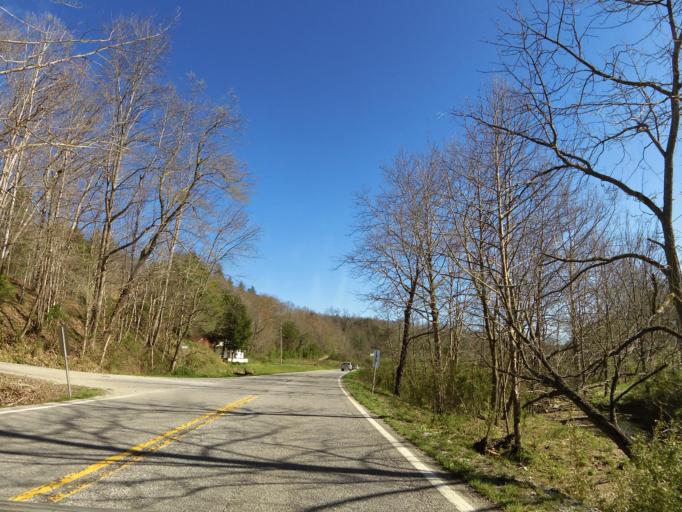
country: US
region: Tennessee
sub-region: Scott County
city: Oneida
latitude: 36.4716
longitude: -84.4800
